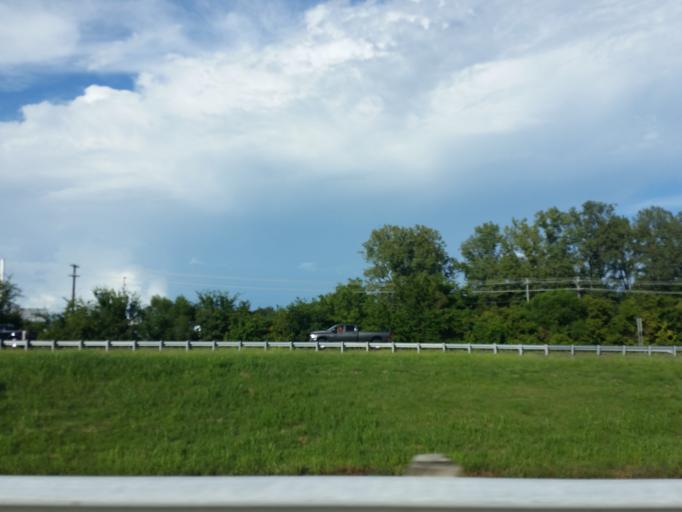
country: US
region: Tennessee
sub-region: Montgomery County
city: Clarksville
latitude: 36.5850
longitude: -87.2698
